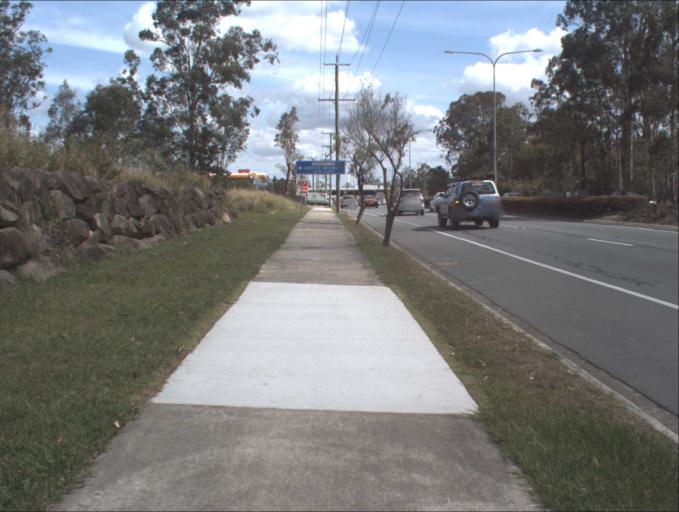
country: AU
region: Queensland
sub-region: Logan
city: Slacks Creek
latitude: -27.6614
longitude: 153.1408
